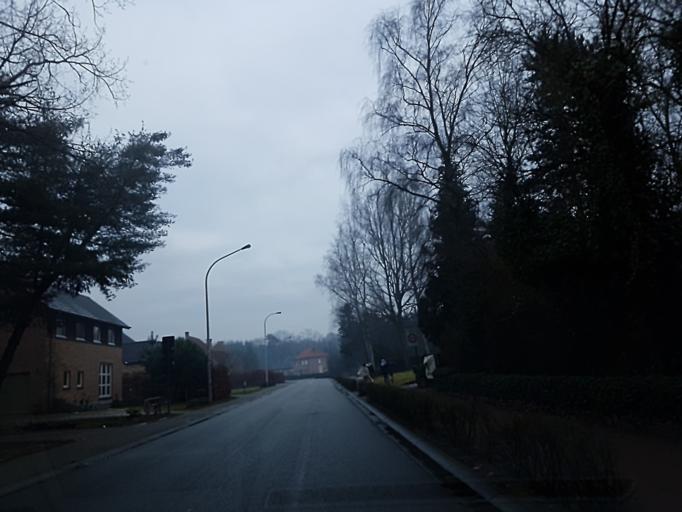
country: BE
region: Flanders
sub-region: Provincie Antwerpen
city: Lier
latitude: 51.1557
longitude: 4.6116
